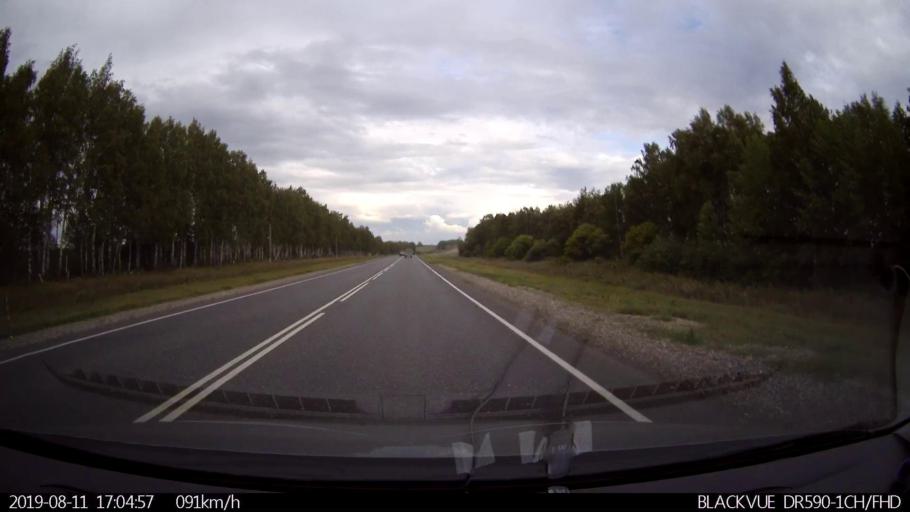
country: RU
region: Ulyanovsk
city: Mayna
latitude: 54.2997
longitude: 47.7750
